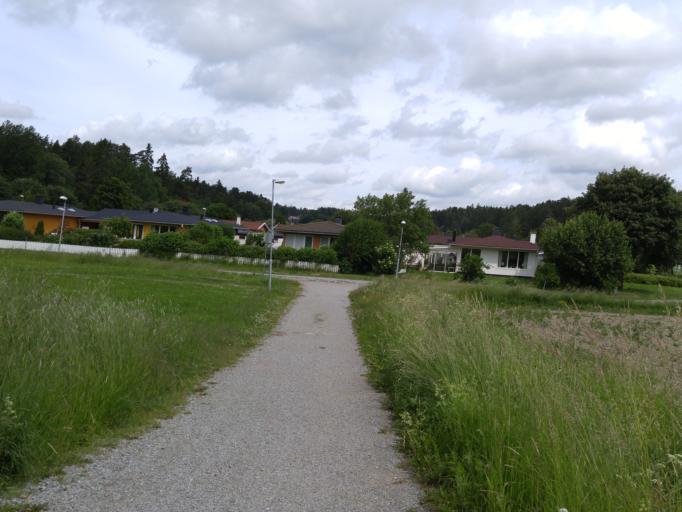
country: SE
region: Stockholm
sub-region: Sigtuna Kommun
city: Sigtuna
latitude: 59.6194
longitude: 17.7051
